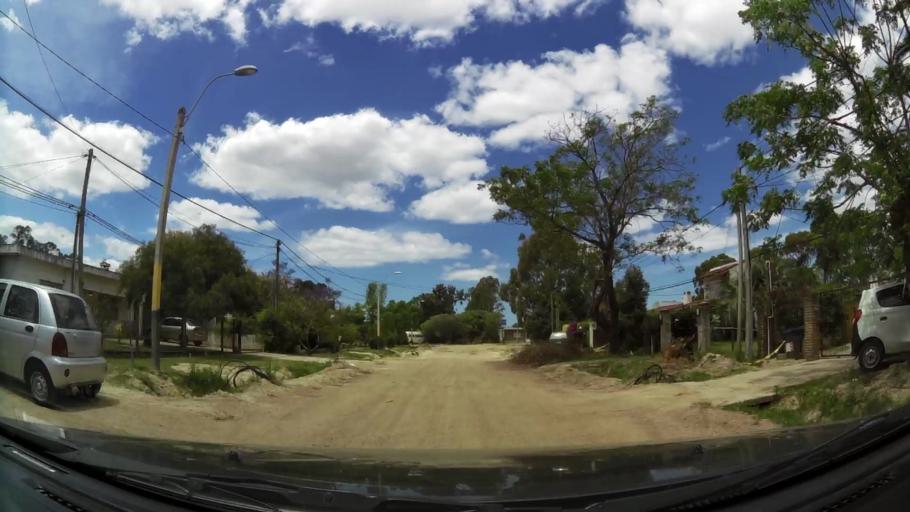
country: UY
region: Canelones
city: Colonia Nicolich
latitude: -34.8318
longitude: -55.9803
